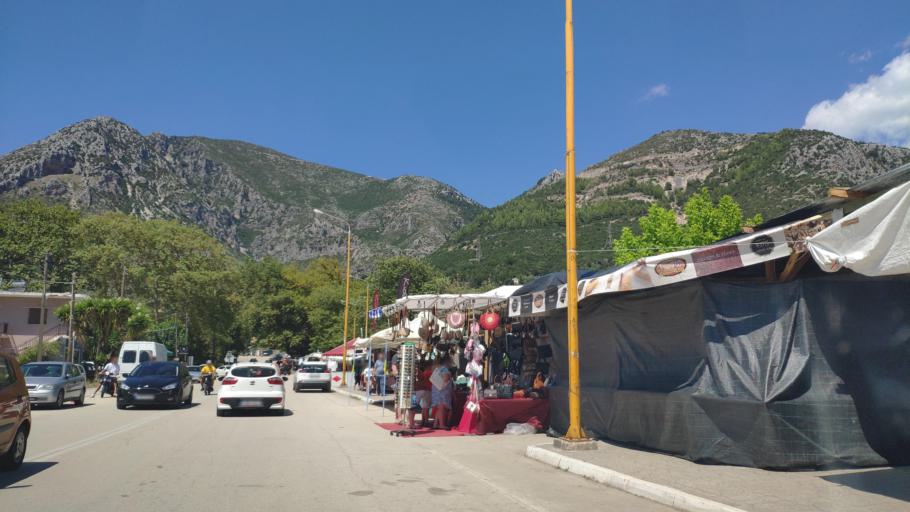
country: GR
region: Epirus
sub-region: Nomos Prevezis
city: Kanalaki
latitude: 39.3246
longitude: 20.6074
